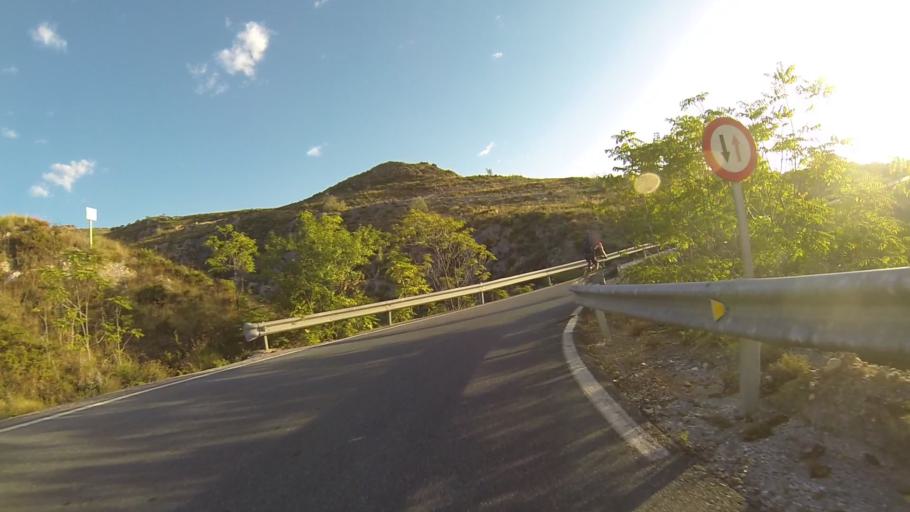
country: ES
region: Andalusia
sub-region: Provincia de Granada
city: Valor
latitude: 36.9783
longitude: -3.1335
